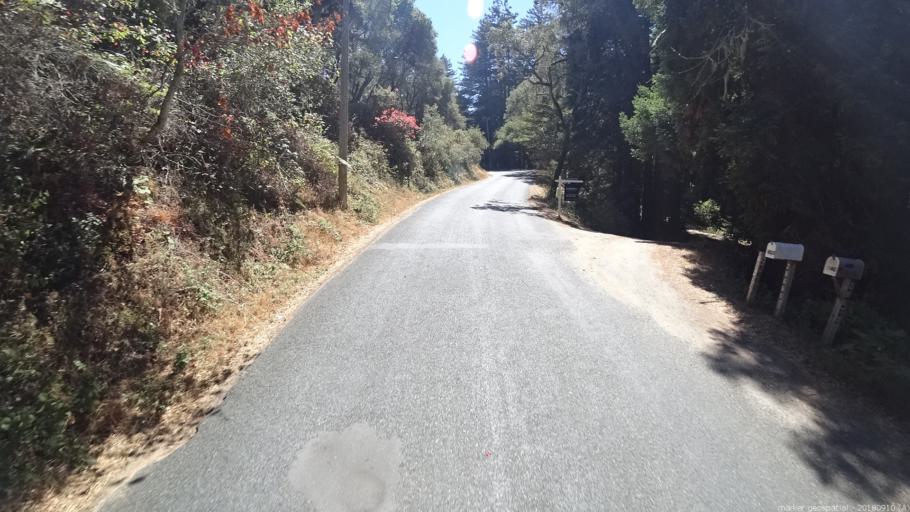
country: US
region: California
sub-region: Monterey County
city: Carmel Valley Village
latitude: 36.5125
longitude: -121.8115
